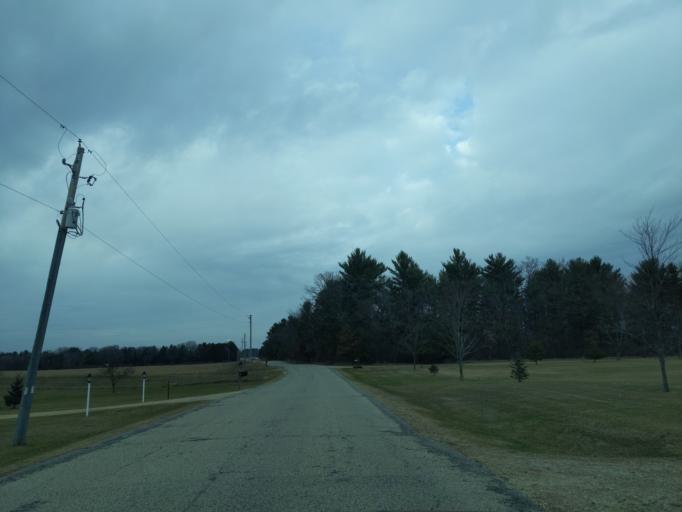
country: US
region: Wisconsin
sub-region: Waushara County
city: Wautoma
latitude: 44.0539
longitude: -89.2776
